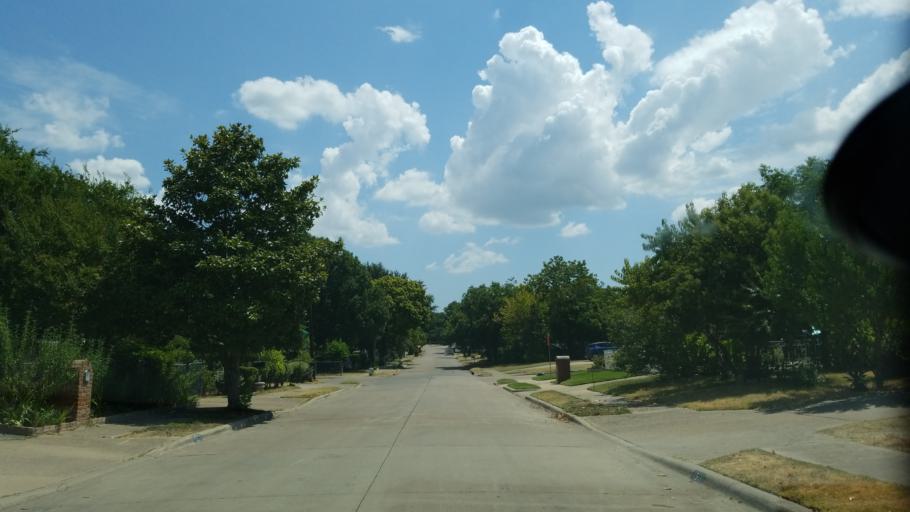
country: US
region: Texas
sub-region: Dallas County
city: Cockrell Hill
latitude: 32.7305
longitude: -96.8956
